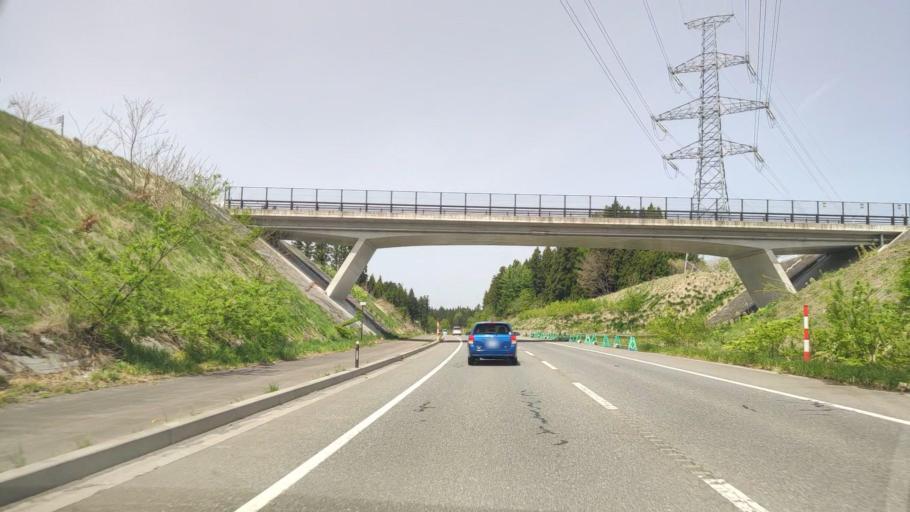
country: JP
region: Aomori
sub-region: Misawa Shi
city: Inuotose
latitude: 40.6849
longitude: 141.1703
